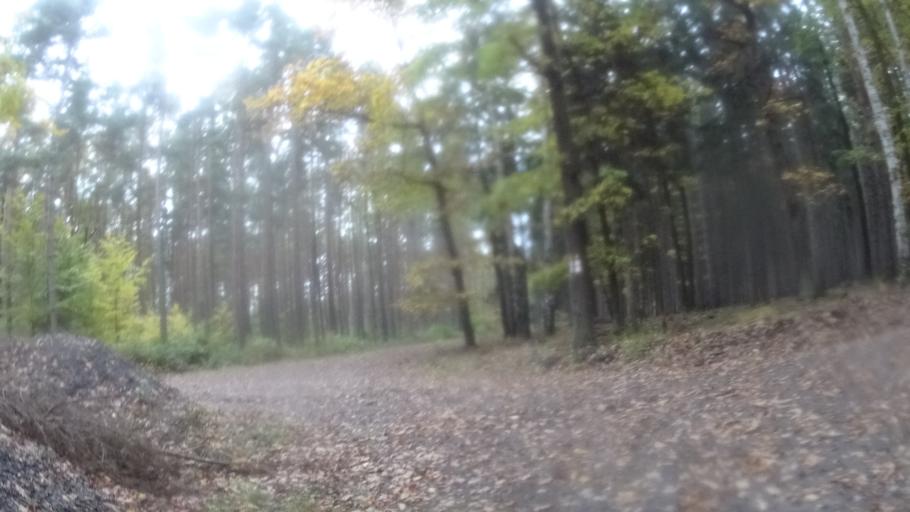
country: DE
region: Thuringia
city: Grosseutersdorf
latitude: 50.7730
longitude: 11.5713
